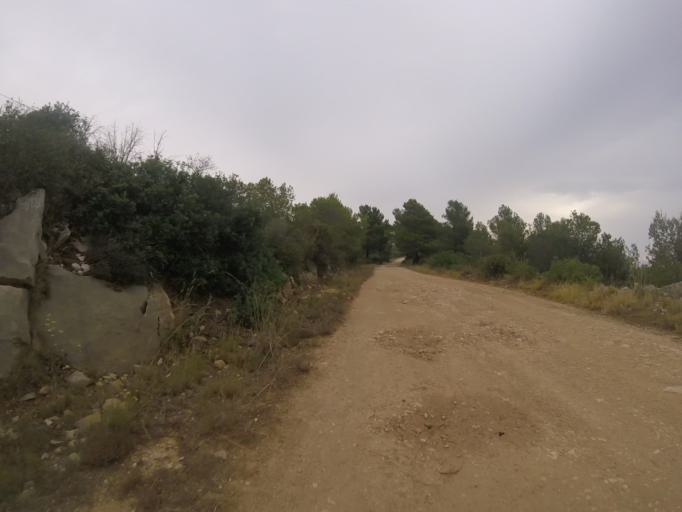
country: ES
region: Valencia
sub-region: Provincia de Castello
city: Alcoceber
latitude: 40.2733
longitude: 0.2782
